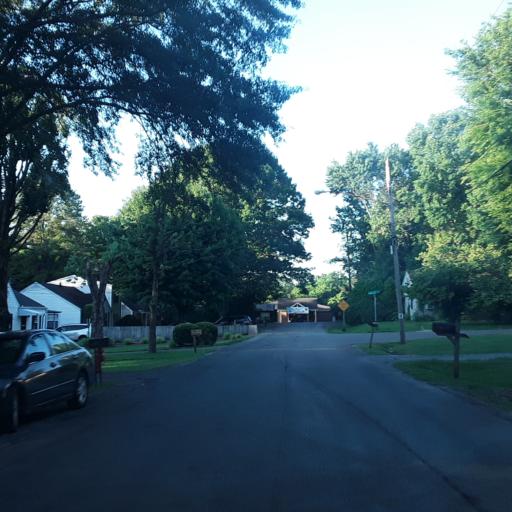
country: US
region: Tennessee
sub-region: Davidson County
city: Oak Hill
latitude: 36.1086
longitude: -86.7335
